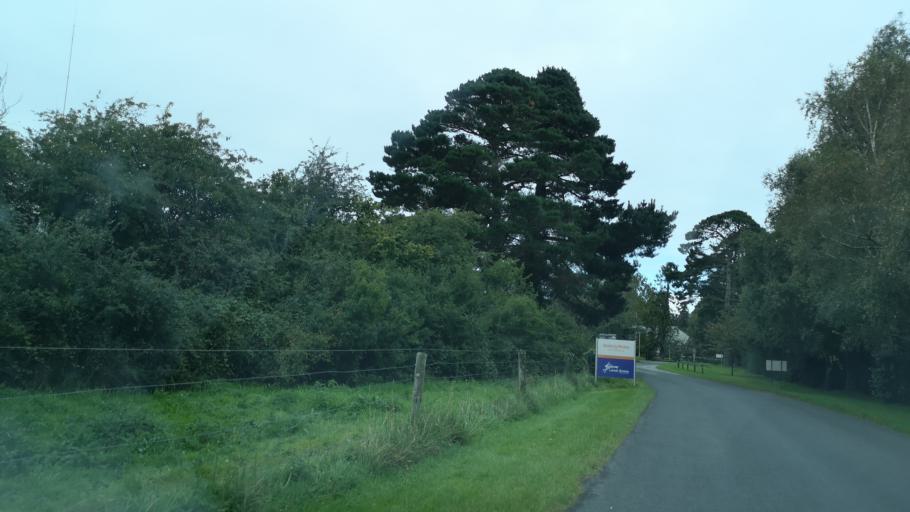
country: IE
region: Leinster
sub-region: Uibh Fhaili
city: Ferbane
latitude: 53.2268
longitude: -7.7291
